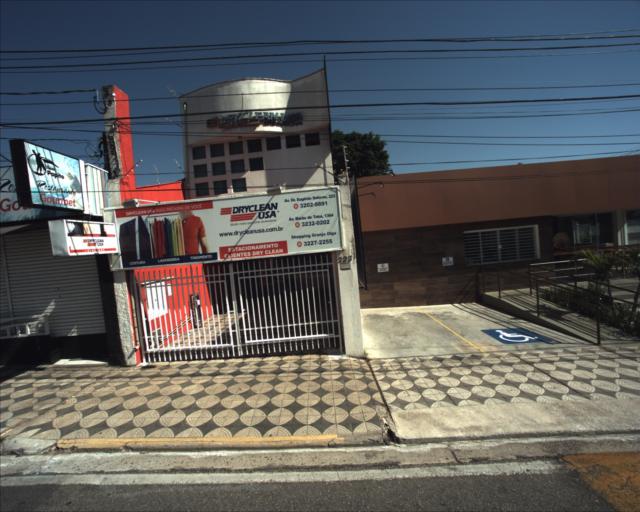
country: BR
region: Sao Paulo
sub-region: Sorocaba
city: Sorocaba
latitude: -23.5007
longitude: -47.4686
